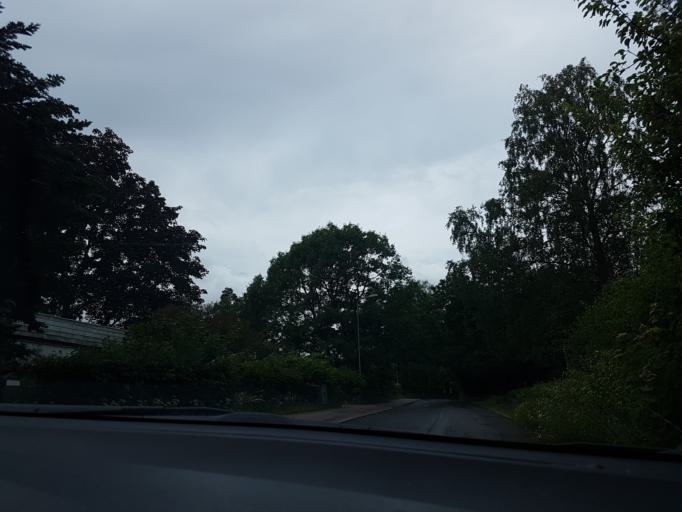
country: FI
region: Uusimaa
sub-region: Helsinki
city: Vantaa
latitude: 60.2298
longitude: 25.1142
